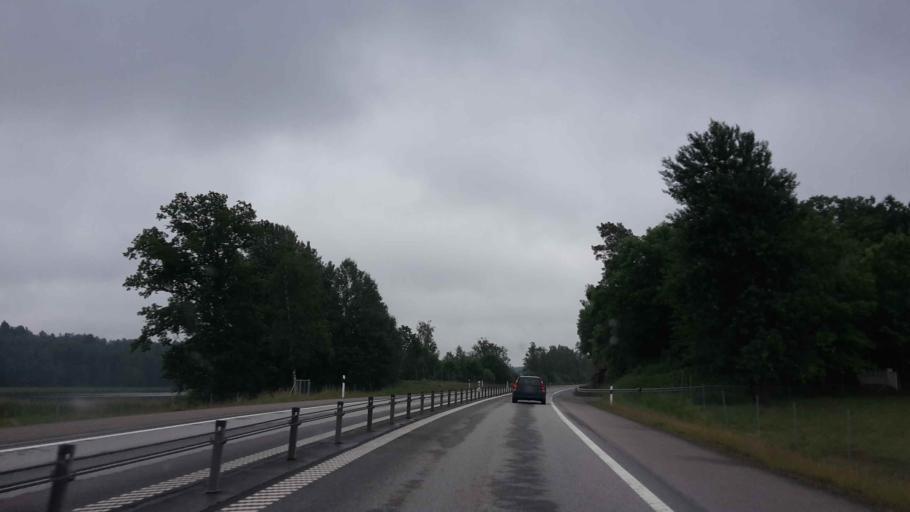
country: SE
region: OEstergoetland
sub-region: Valdemarsviks Kommun
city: Gusum
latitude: 58.3281
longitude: 16.4722
